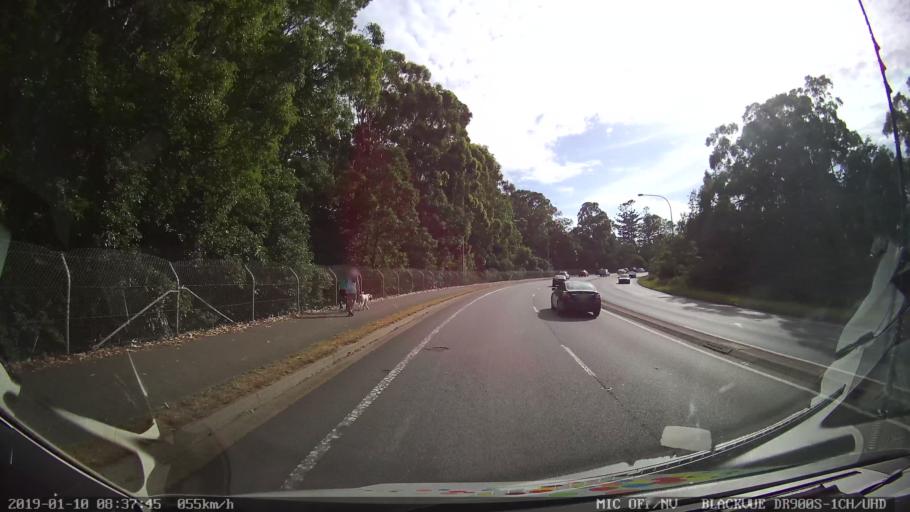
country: AU
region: New South Wales
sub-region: Coffs Harbour
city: Coffs Harbour
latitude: -30.3039
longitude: 153.1028
